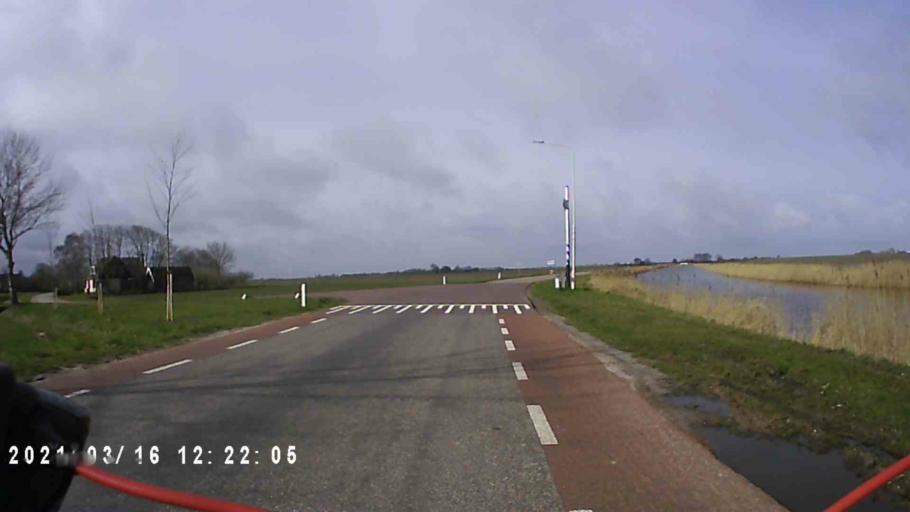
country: NL
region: Friesland
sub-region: Gemeente Ferwerderadiel
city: Hallum
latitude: 53.3056
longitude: 5.7602
